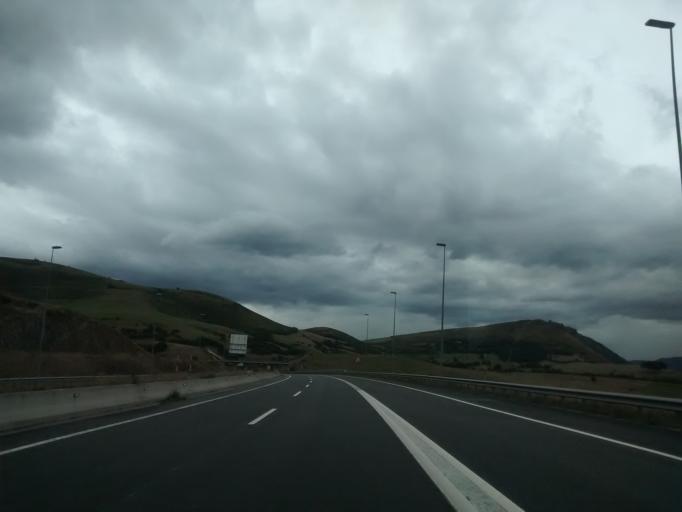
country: ES
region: Cantabria
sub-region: Provincia de Cantabria
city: Santiurde de Reinosa
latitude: 43.0713
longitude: -4.0858
